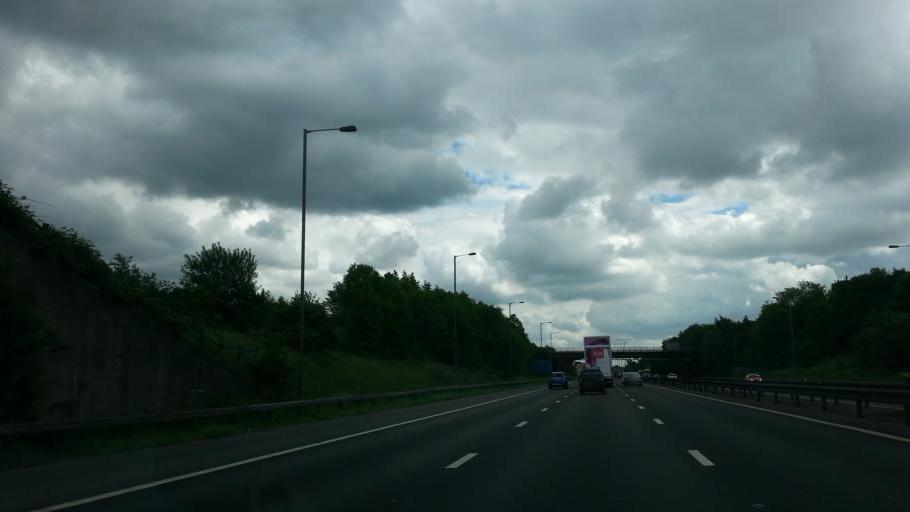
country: GB
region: England
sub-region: Staffordshire
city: Essington
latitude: 52.6365
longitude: -2.0527
